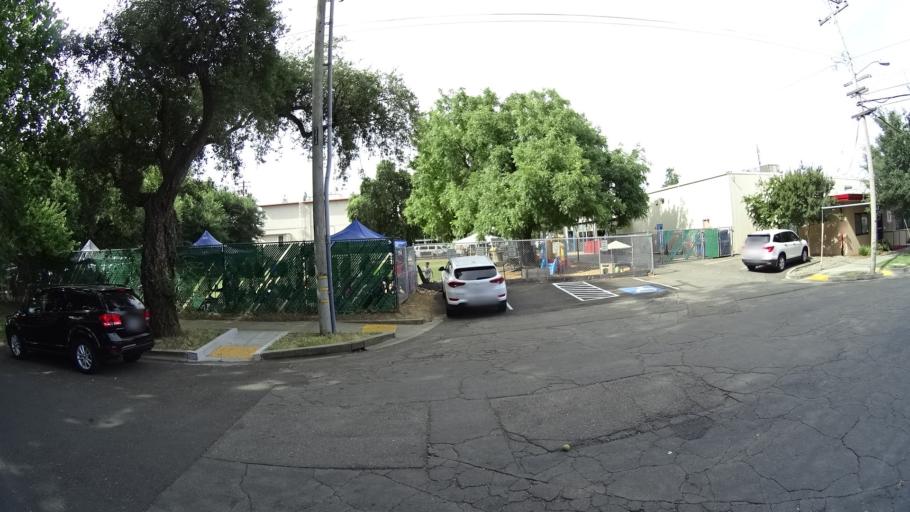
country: US
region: California
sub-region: Sacramento County
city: Sacramento
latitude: 38.5635
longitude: -121.4855
